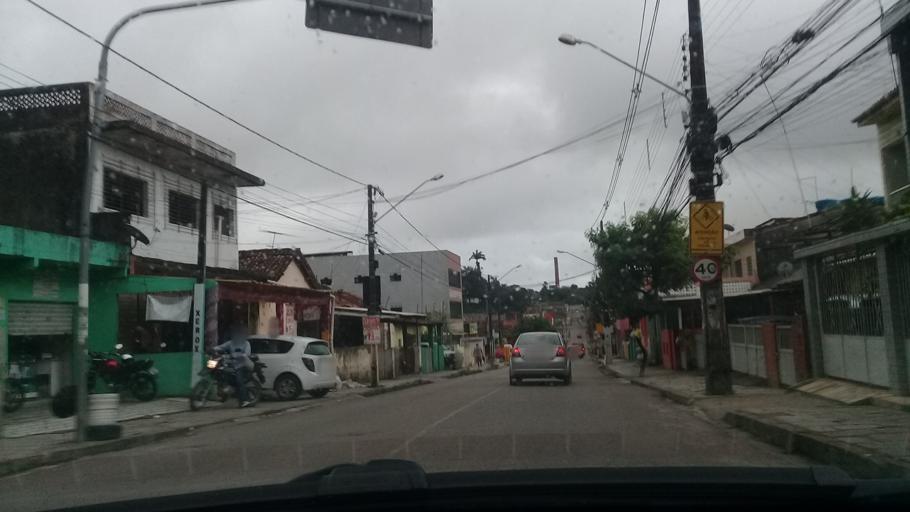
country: BR
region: Pernambuco
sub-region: Moreno
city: Moreno
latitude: -8.1179
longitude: -35.0947
